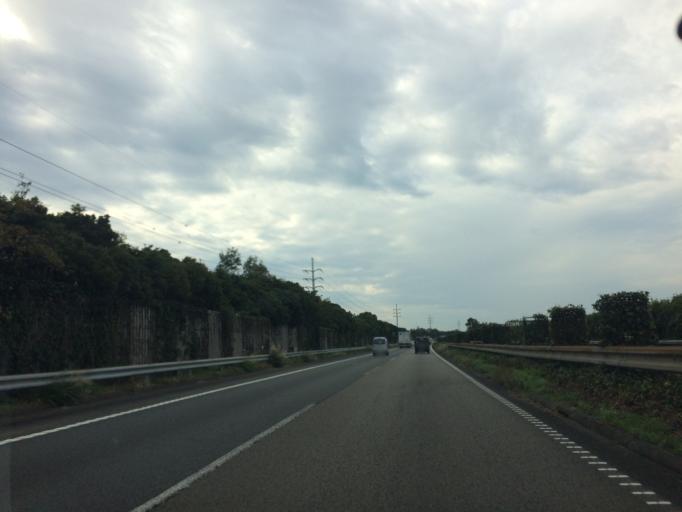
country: JP
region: Shizuoka
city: Fujieda
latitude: 34.8486
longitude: 138.2822
